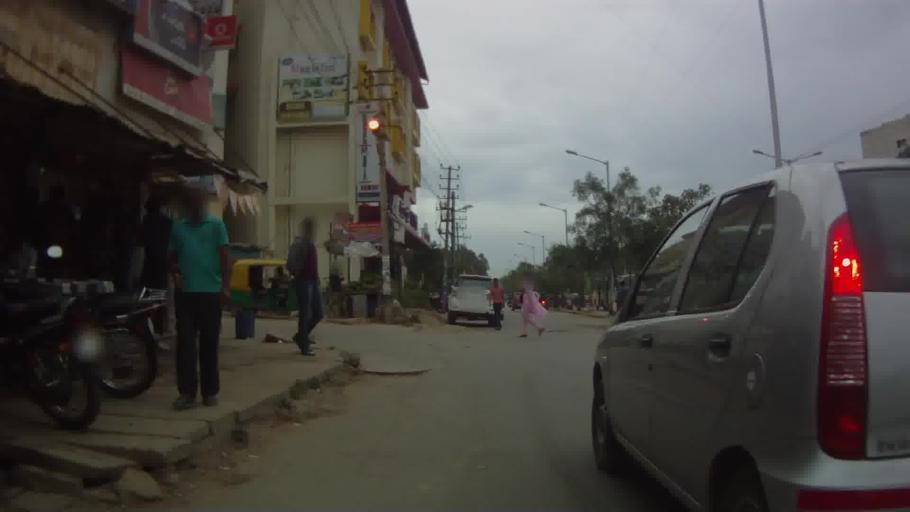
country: IN
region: Karnataka
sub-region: Bangalore Urban
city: Bangalore
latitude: 12.9790
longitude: 77.6953
